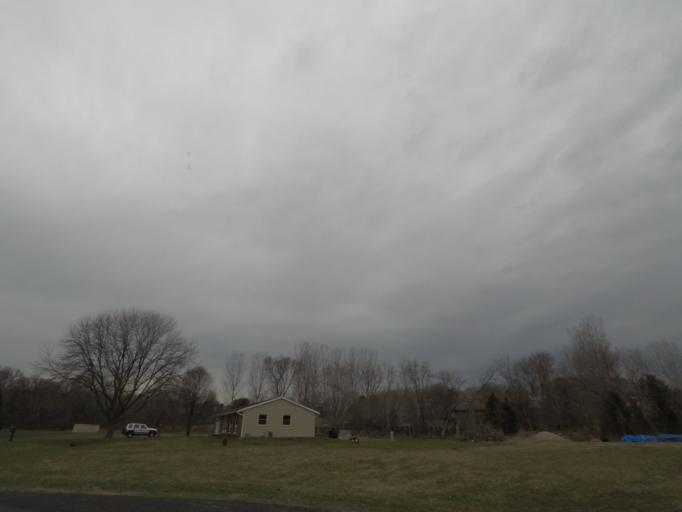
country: US
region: Wisconsin
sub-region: Dane County
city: Middleton
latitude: 43.1104
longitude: -89.5476
